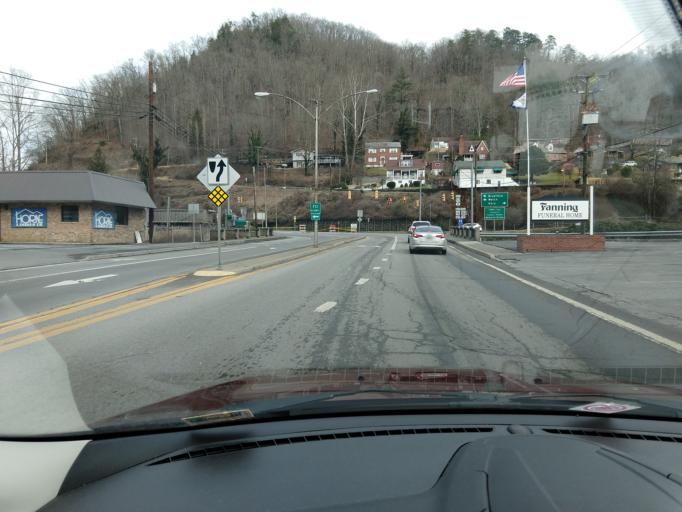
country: US
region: West Virginia
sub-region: McDowell County
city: Welch
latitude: 37.4168
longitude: -81.5905
